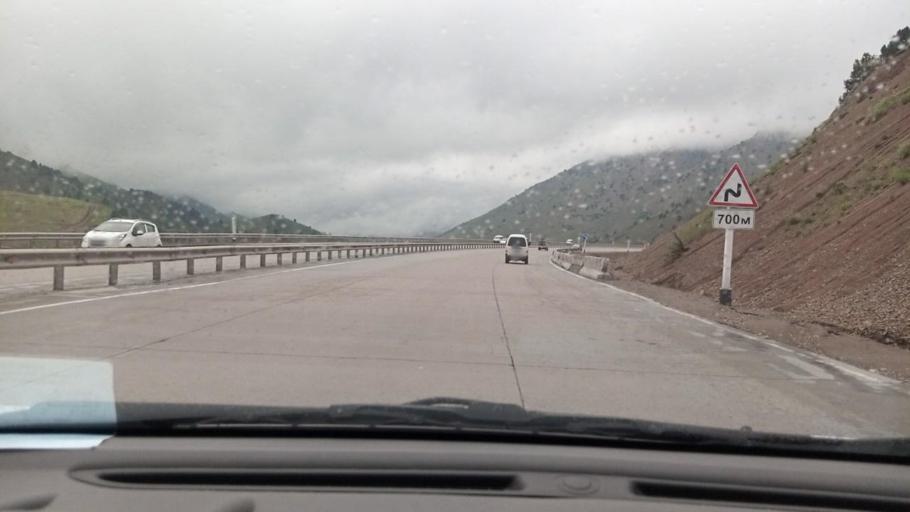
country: UZ
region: Toshkent
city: Angren
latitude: 41.1079
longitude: 70.5026
